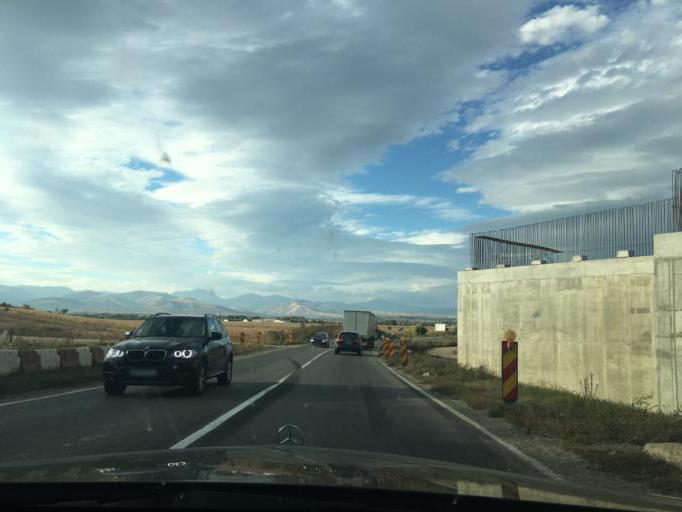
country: RO
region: Alba
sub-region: Comuna Santimbru
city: Santimbru
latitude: 46.1478
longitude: 23.6447
